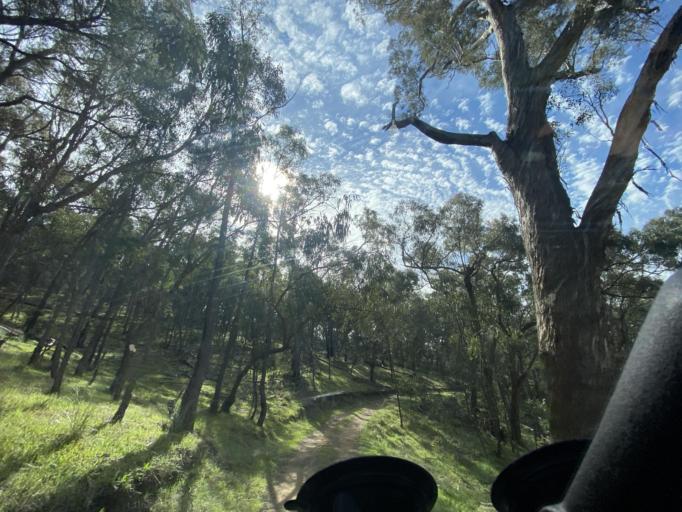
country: AU
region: Victoria
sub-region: Mansfield
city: Mansfield
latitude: -36.8062
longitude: 146.1193
